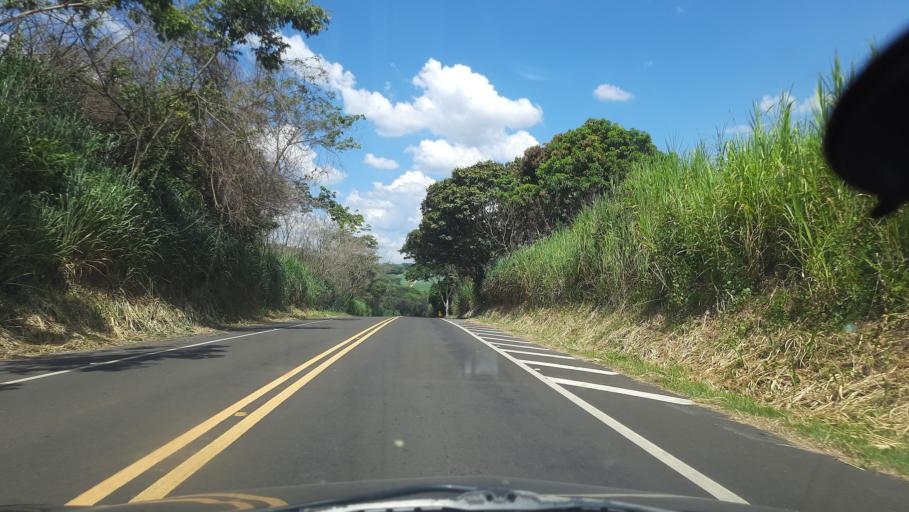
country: BR
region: Sao Paulo
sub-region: Sao Jose Do Rio Pardo
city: Sao Jose do Rio Pardo
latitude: -21.5933
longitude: -46.9908
